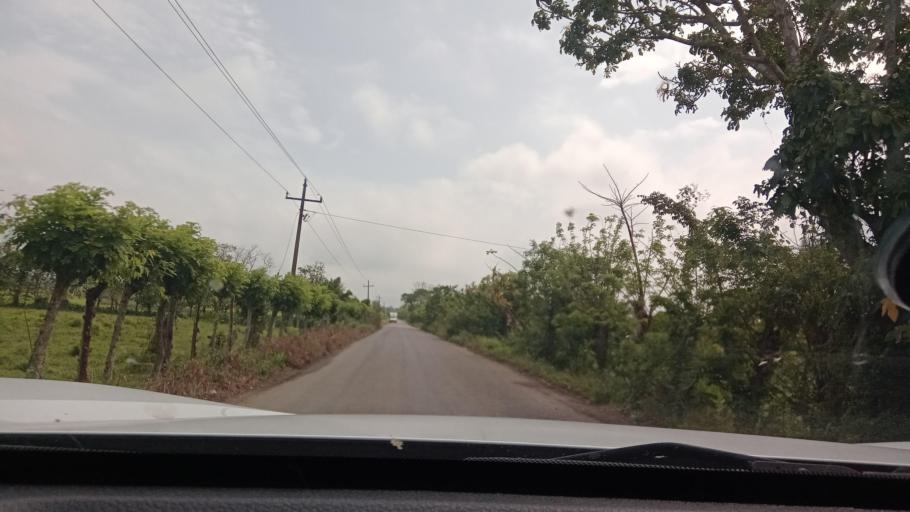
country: MX
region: Tabasco
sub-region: Huimanguillo
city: Francisco Rueda
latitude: 17.5532
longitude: -94.1232
